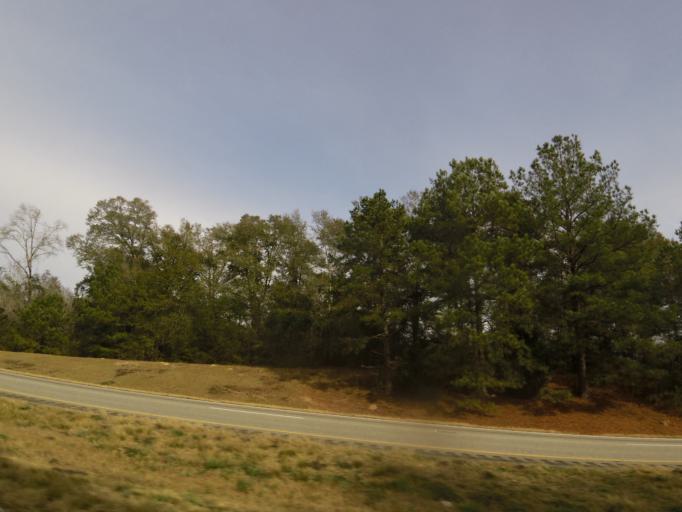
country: US
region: Alabama
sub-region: Dale County
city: Ozark
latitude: 31.4099
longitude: -85.6012
